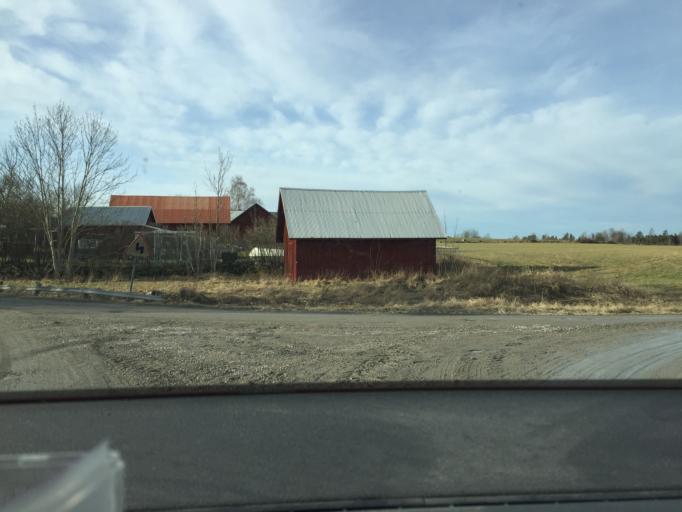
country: SE
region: OErebro
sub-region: Hallsbergs Kommun
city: Skollersta
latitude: 59.1352
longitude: 15.4170
